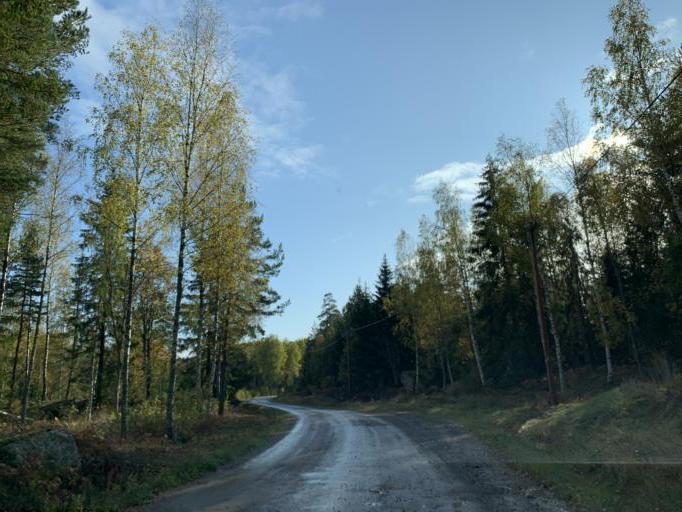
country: SE
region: Soedermanland
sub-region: Eskilstuna Kommun
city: Kvicksund
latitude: 59.3693
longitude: 16.2642
